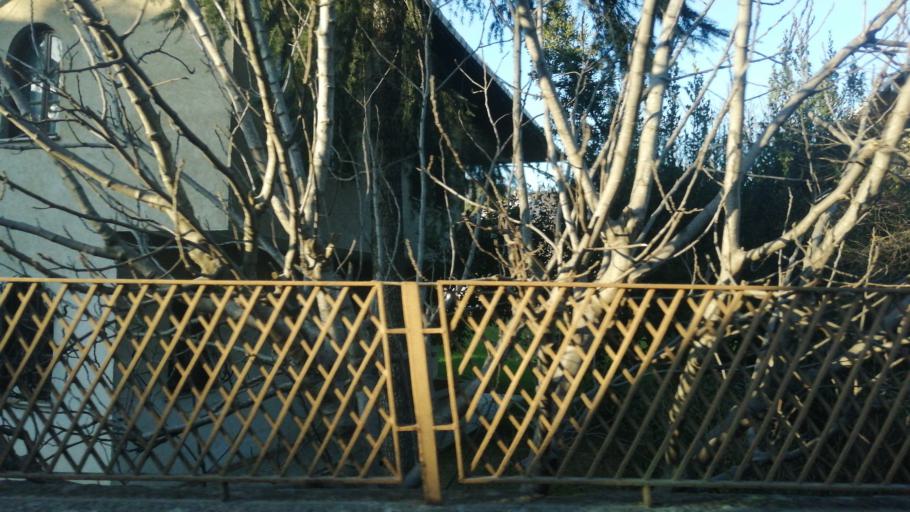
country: TR
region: Istanbul
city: UEskuedar
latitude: 41.0494
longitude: 29.0562
